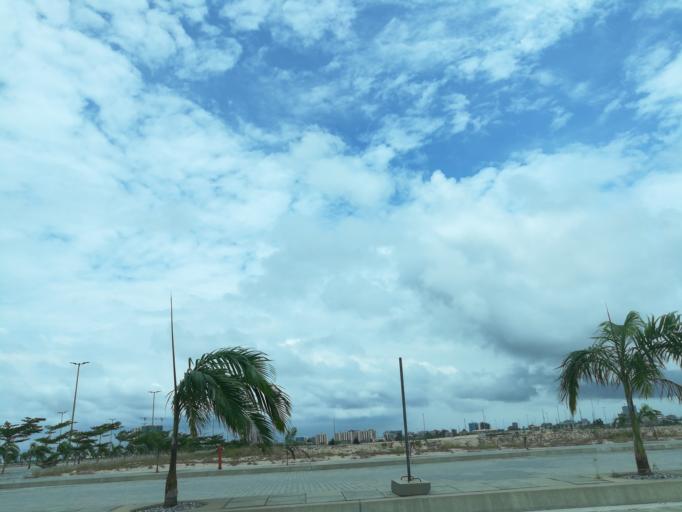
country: NG
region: Lagos
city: Ikoyi
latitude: 6.4095
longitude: 3.4185
